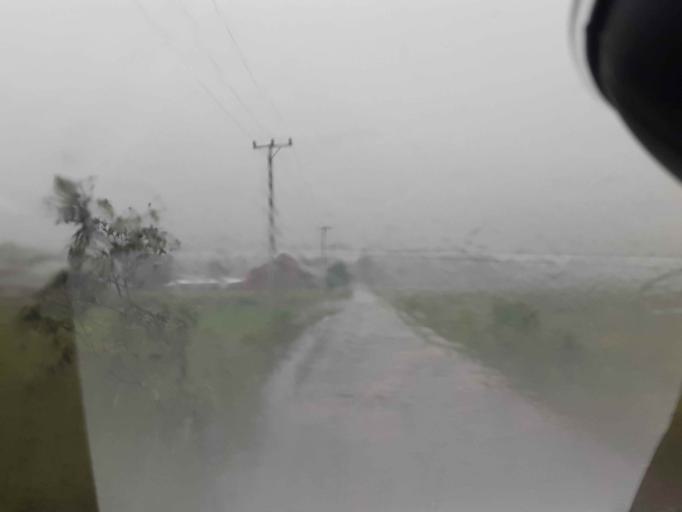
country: ID
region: Lampung
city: Kedaton
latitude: -5.3897
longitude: 105.3239
